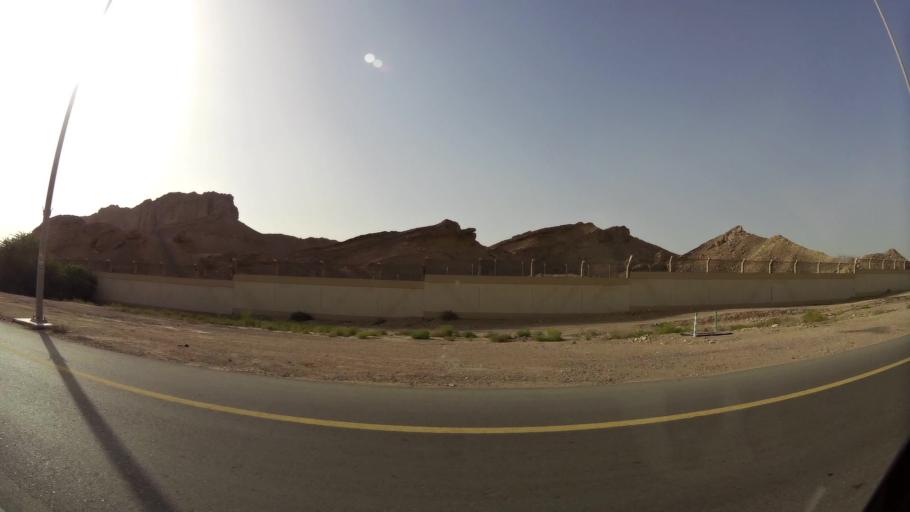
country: AE
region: Abu Dhabi
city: Al Ain
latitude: 24.1112
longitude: 55.7466
